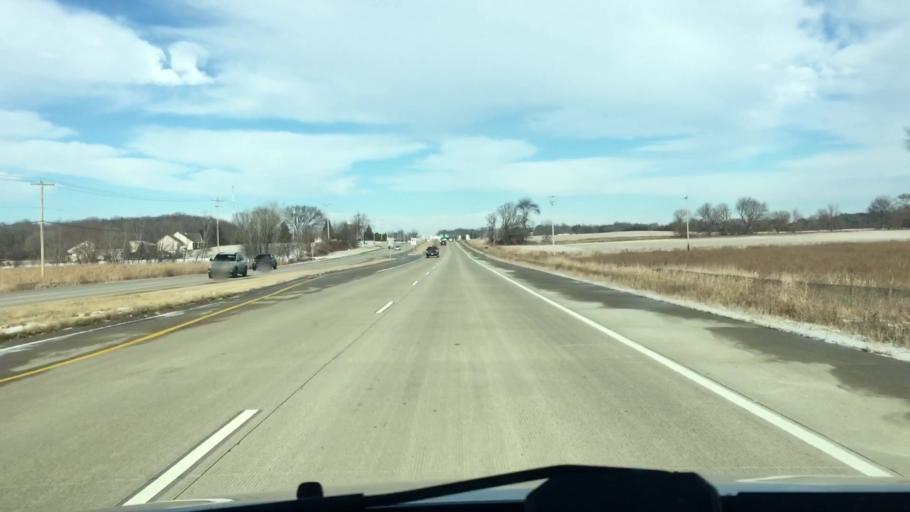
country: US
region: Wisconsin
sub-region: Waukesha County
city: Mukwonago
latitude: 42.9140
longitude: -88.3455
